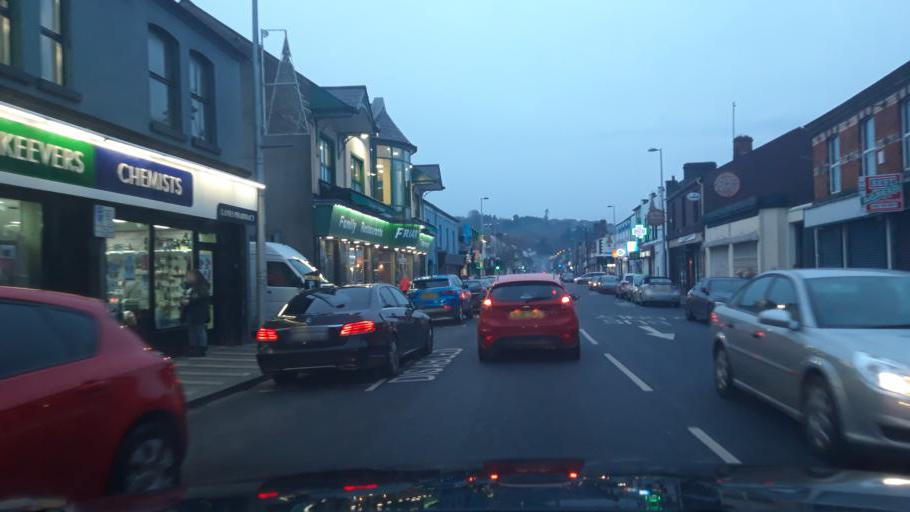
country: GB
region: Northern Ireland
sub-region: Newry and Mourne District
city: Newry
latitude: 54.1767
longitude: -6.3402
